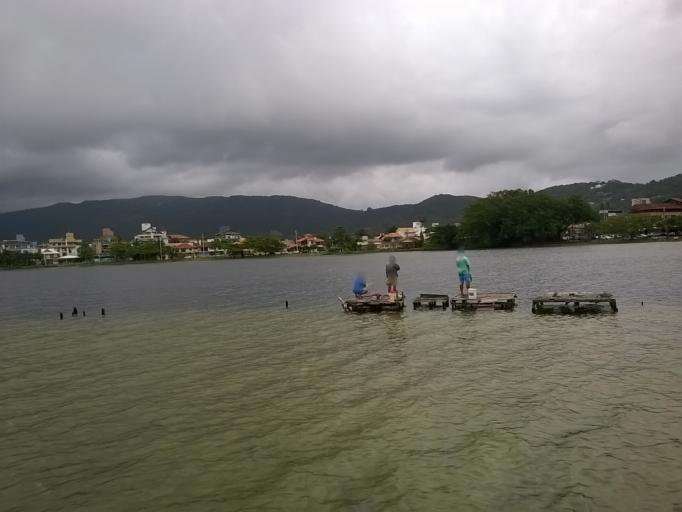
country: BR
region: Santa Catarina
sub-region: Florianopolis
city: Lagoa
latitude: -27.6057
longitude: -48.4637
